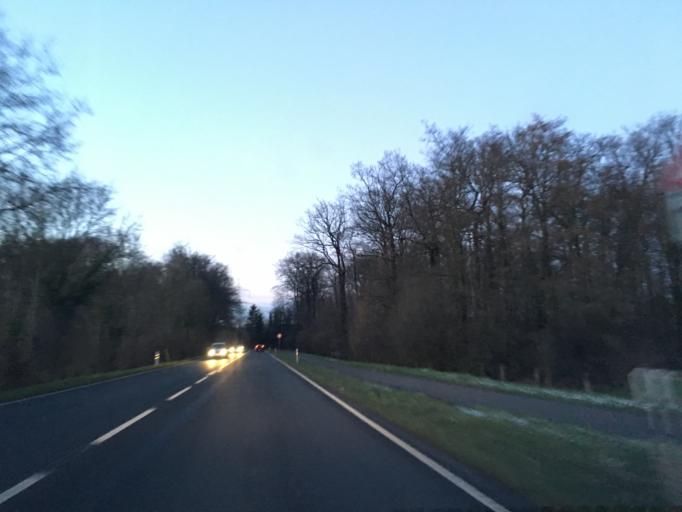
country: DE
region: North Rhine-Westphalia
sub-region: Regierungsbezirk Munster
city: Muenster
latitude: 51.8721
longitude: 7.6556
